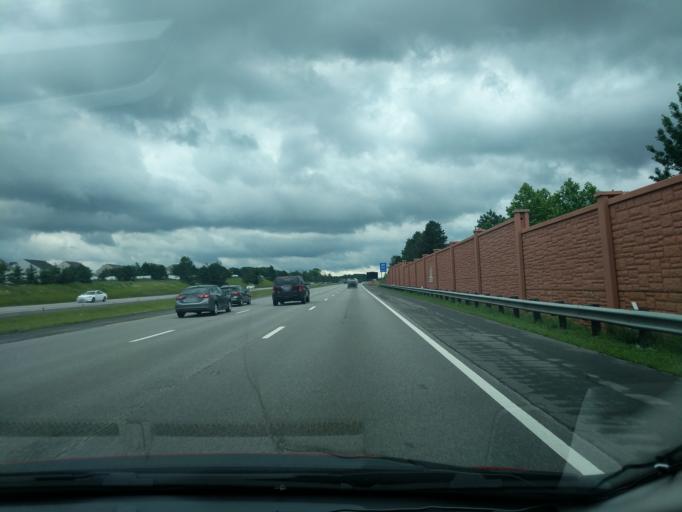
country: US
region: Ohio
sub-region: Cuyahoga County
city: Strongsville
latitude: 41.2741
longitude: -81.8061
